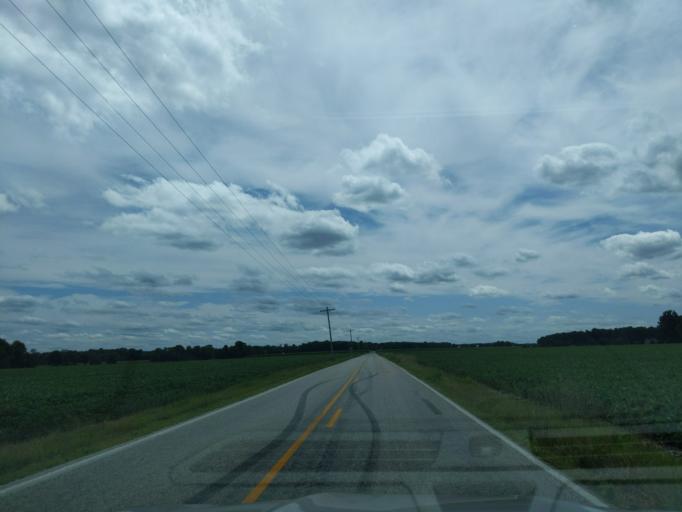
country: US
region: Indiana
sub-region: Ripley County
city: Batesville
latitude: 39.2340
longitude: -85.2679
